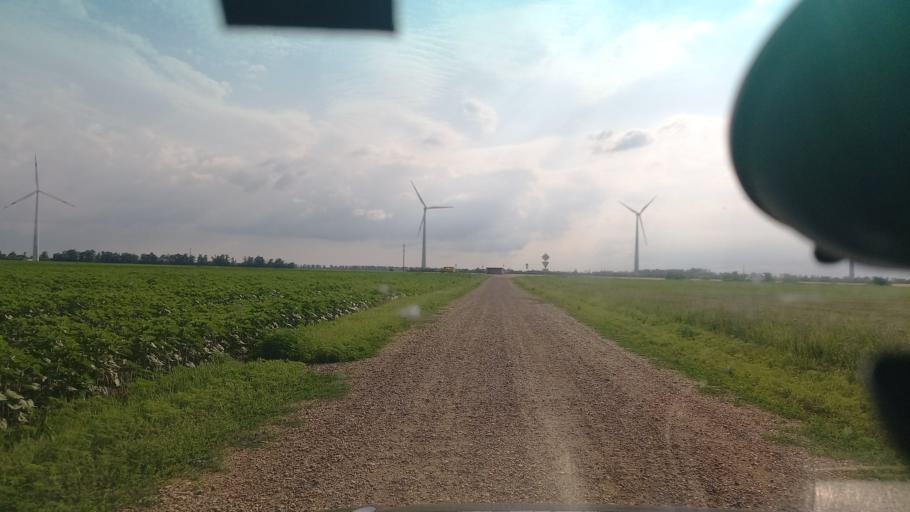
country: RU
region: Adygeya
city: Giaginskaya
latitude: 44.9524
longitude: 40.0865
